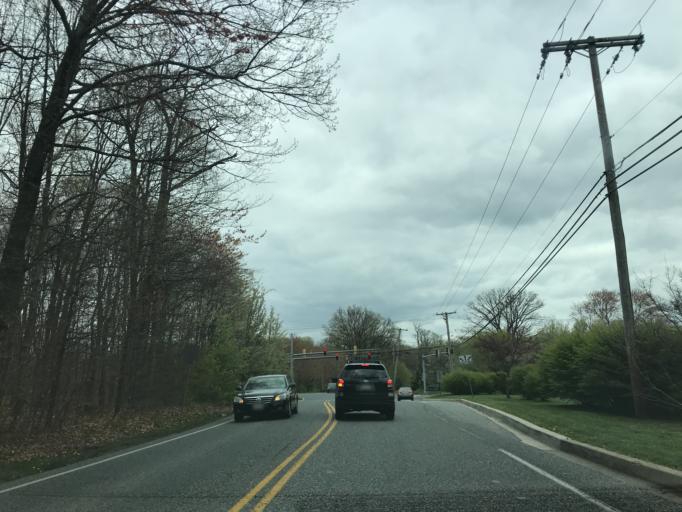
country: US
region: Maryland
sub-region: Harford County
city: Bel Air South
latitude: 39.5238
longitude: -76.2871
